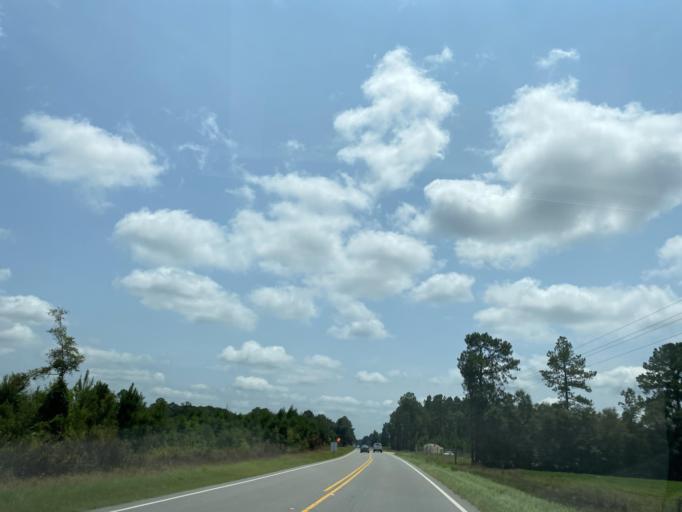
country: US
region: Georgia
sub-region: Jeff Davis County
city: Hazlehurst
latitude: 31.7950
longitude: -82.5656
